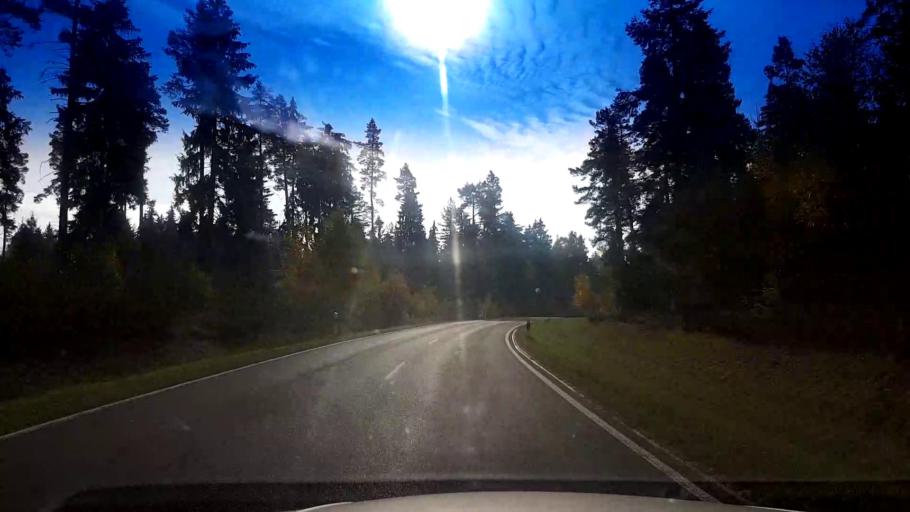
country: DE
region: Bavaria
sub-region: Upper Franconia
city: Schirnding
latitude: 50.0649
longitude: 12.2487
